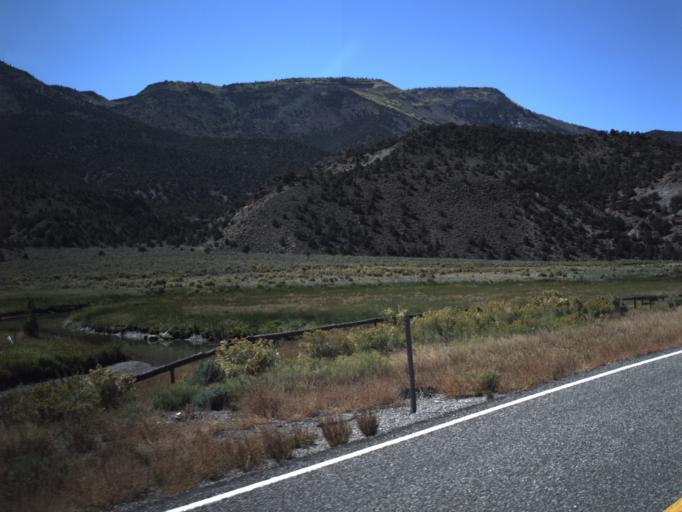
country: US
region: Utah
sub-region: Piute County
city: Junction
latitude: 38.1780
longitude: -112.0752
